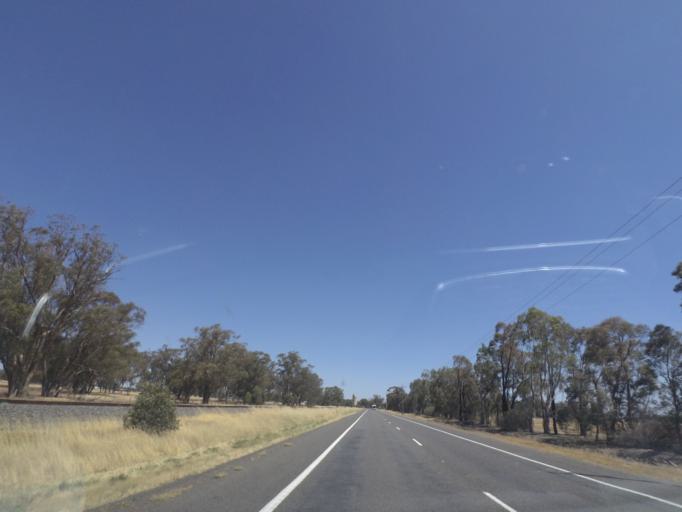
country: AU
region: Victoria
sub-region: Greater Shepparton
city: Shepparton
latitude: -36.2299
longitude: 145.4318
